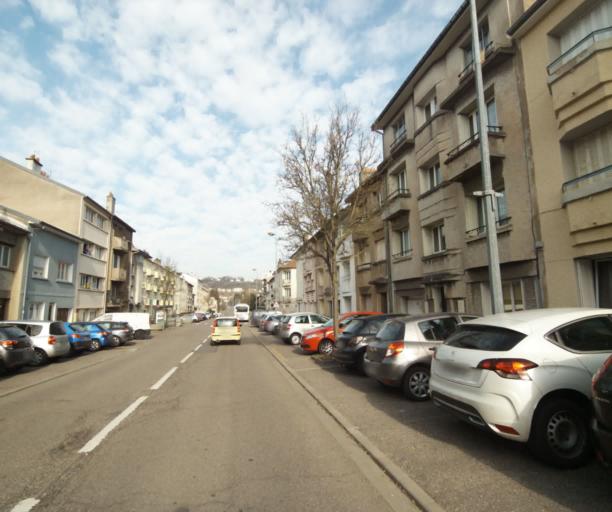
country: FR
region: Lorraine
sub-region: Departement de Meurthe-et-Moselle
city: Villers-les-Nancy
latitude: 48.6778
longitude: 6.1559
